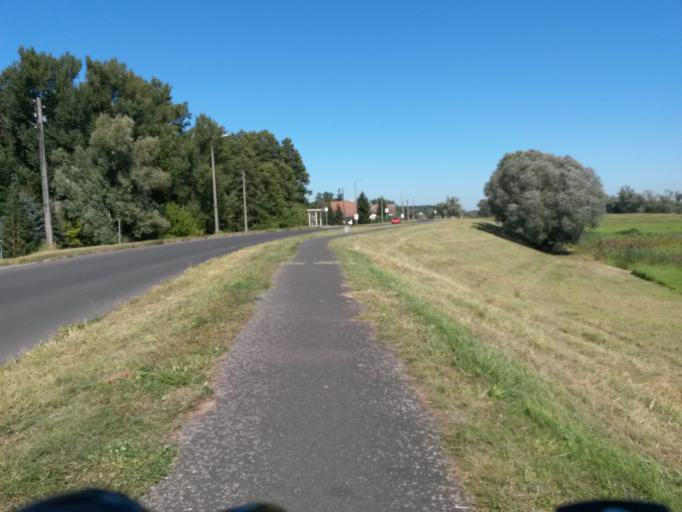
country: DE
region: Brandenburg
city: Oderberg
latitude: 52.8487
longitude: 14.1235
